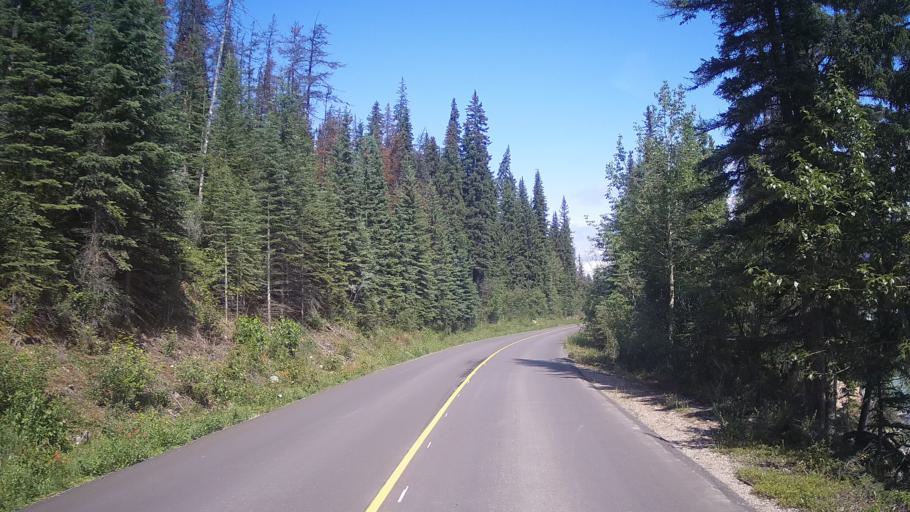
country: CA
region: Alberta
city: Jasper Park Lodge
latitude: 52.7363
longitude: -117.9567
